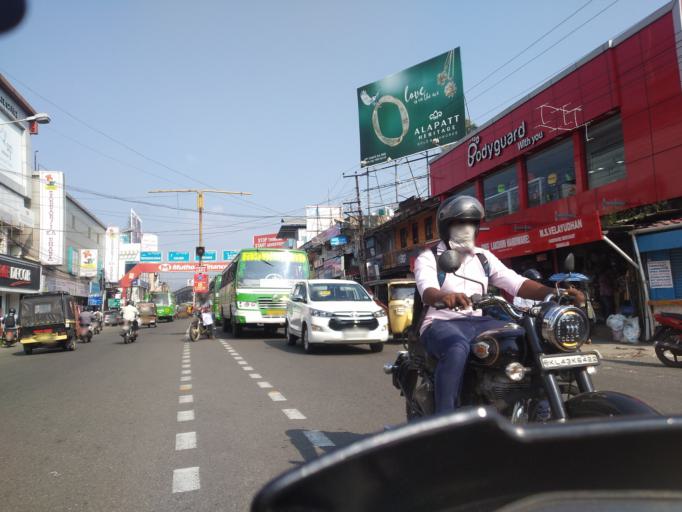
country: IN
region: Kerala
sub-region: Ernakulam
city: Cochin
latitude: 9.9855
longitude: 76.2800
